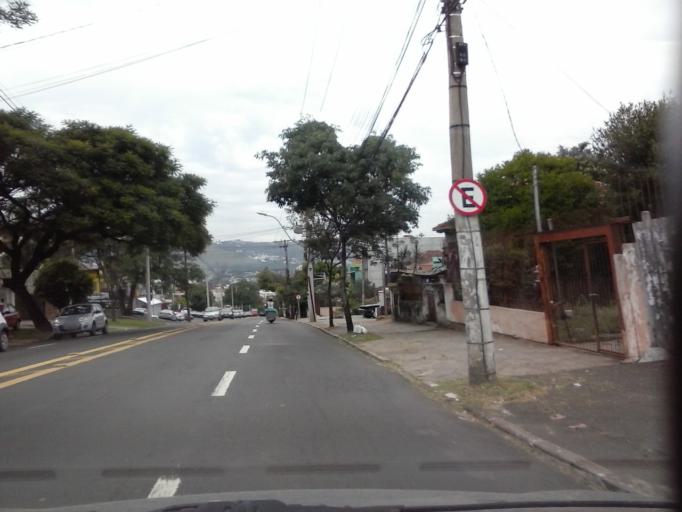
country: BR
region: Rio Grande do Sul
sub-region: Porto Alegre
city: Porto Alegre
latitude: -30.0628
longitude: -51.2063
